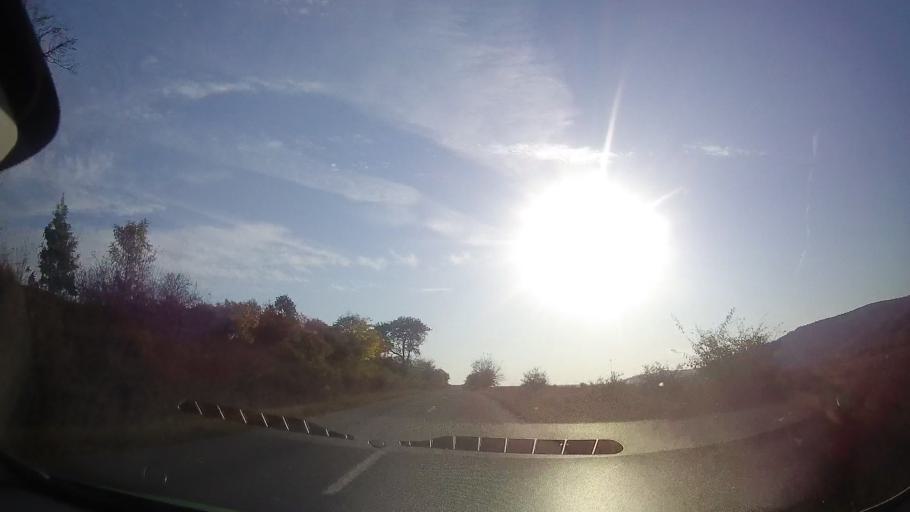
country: RO
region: Timis
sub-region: Comuna Bogda
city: Bogda
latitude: 45.9817
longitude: 21.5605
